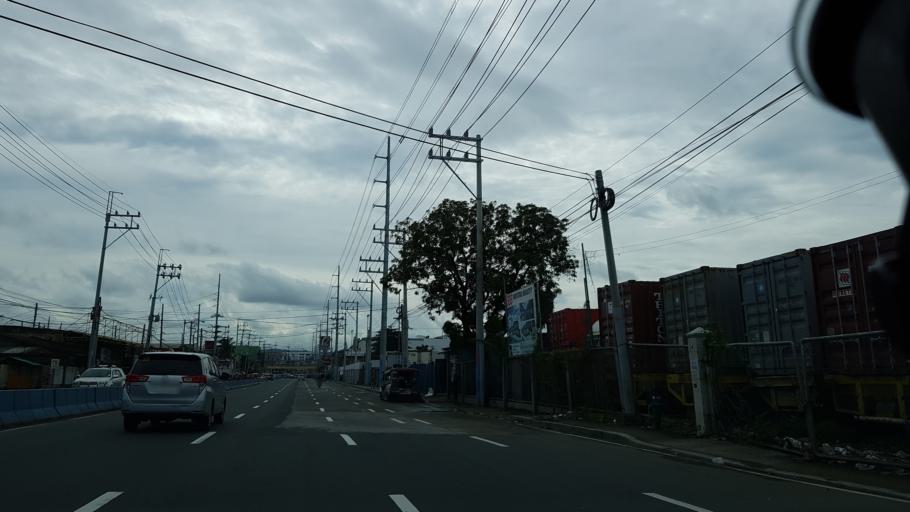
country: PH
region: Calabarzon
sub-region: Province of Rizal
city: Cainta
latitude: 14.5875
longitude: 121.1096
